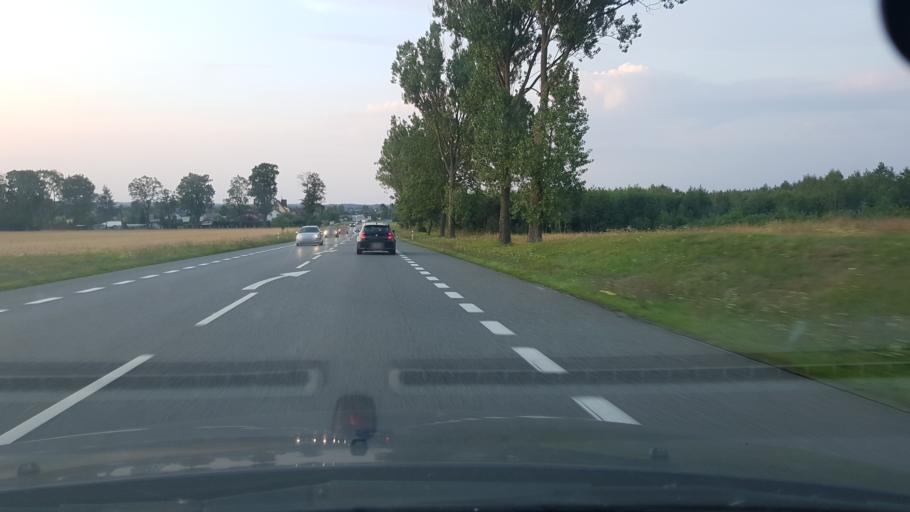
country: PL
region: Masovian Voivodeship
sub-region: Powiat mlawski
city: Mlawa
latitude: 53.1584
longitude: 20.4099
